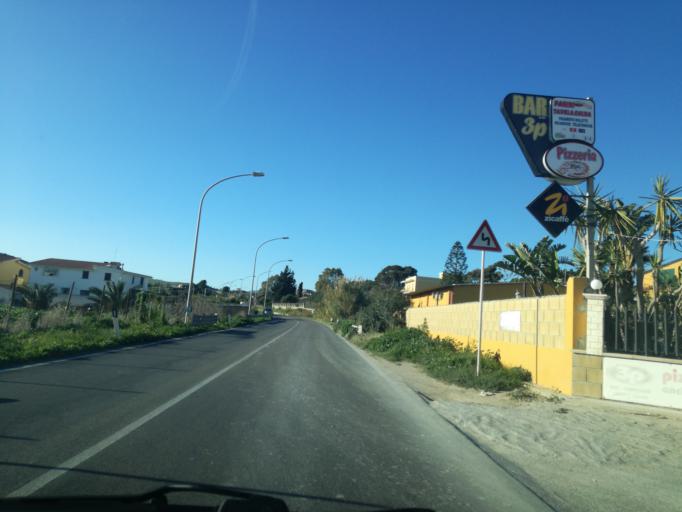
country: IT
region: Sicily
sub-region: Provincia di Caltanissetta
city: Gela
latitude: 37.0996
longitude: 14.1614
